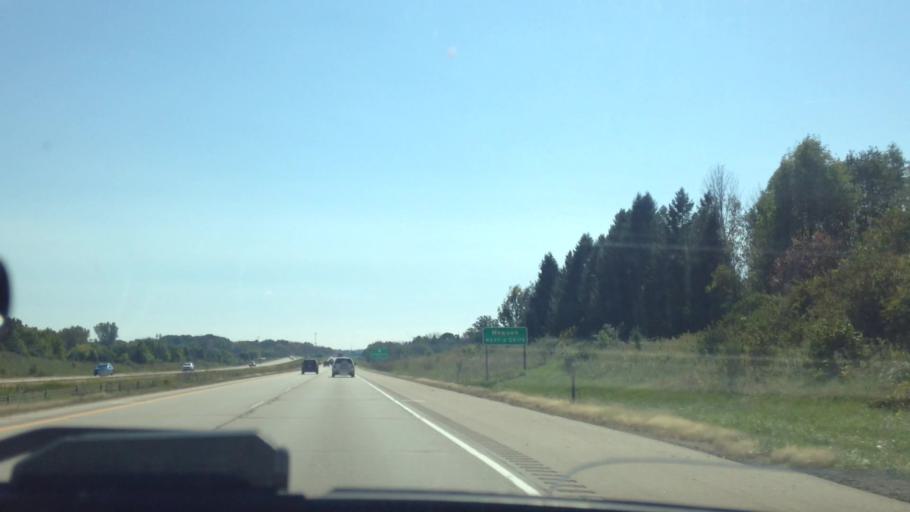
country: US
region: Wisconsin
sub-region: Ozaukee County
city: Grafton
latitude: 43.3015
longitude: -87.9208
